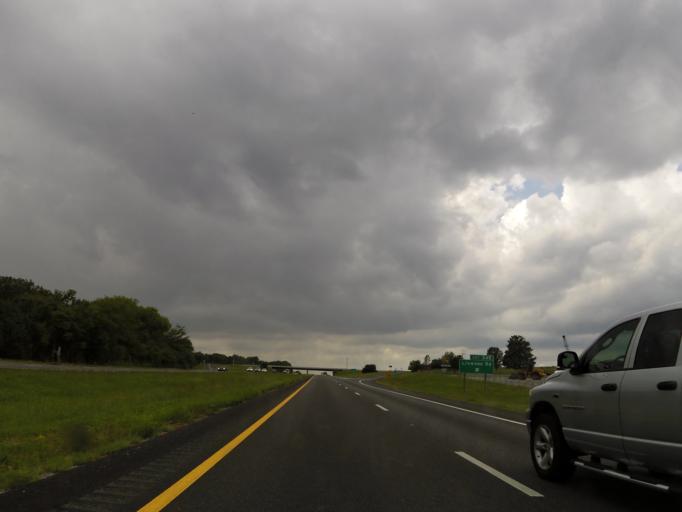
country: US
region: Tennessee
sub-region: Wilson County
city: Watertown
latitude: 36.1900
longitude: -86.1719
